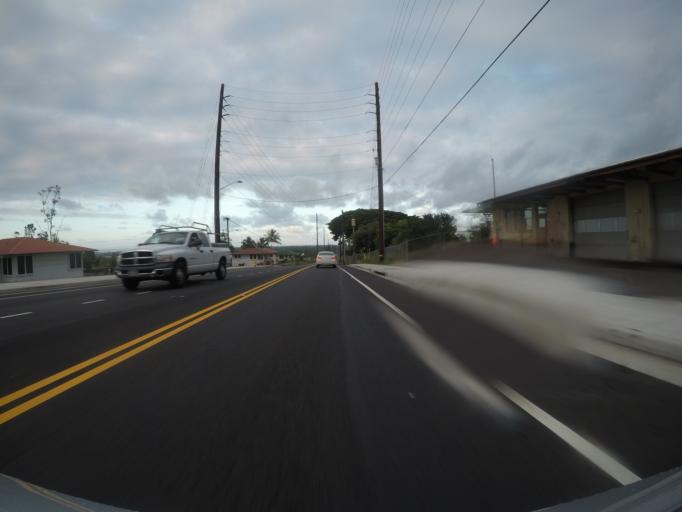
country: US
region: Hawaii
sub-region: Hawaii County
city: Hilo
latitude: 19.6839
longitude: -155.0797
